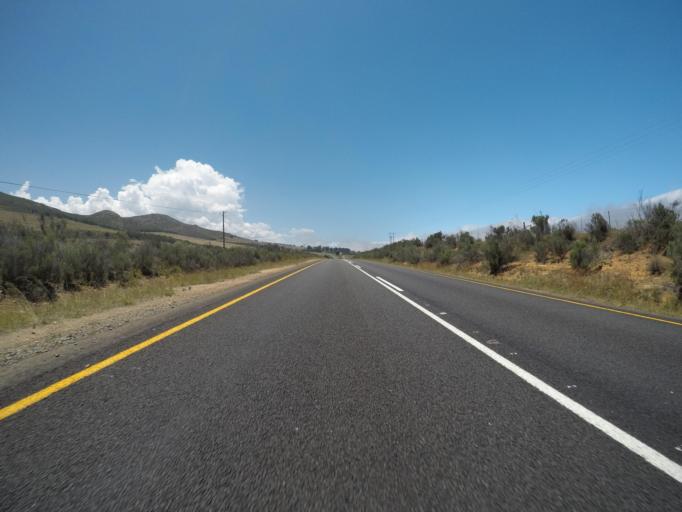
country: ZA
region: Western Cape
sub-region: Eden District Municipality
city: Knysna
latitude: -33.7332
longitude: 23.1108
